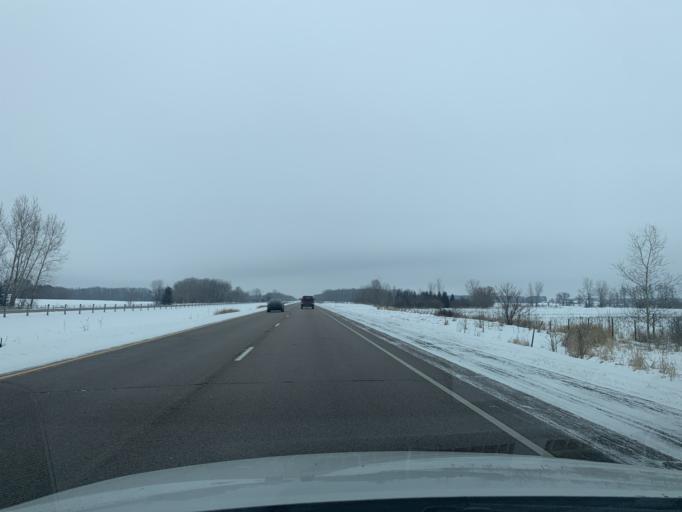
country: US
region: Minnesota
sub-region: Chisago County
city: Rush City
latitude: 45.6442
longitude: -92.9921
